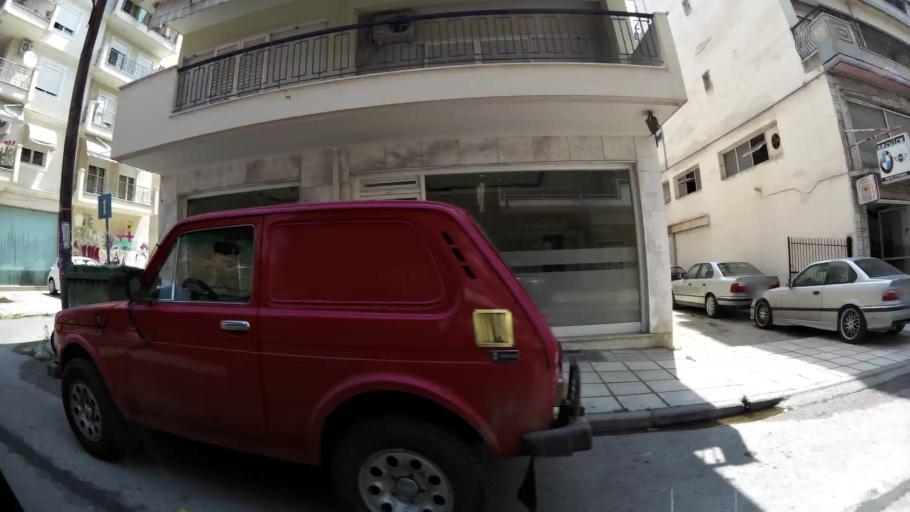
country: GR
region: Central Macedonia
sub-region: Nomos Thessalonikis
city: Evosmos
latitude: 40.6719
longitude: 22.9096
